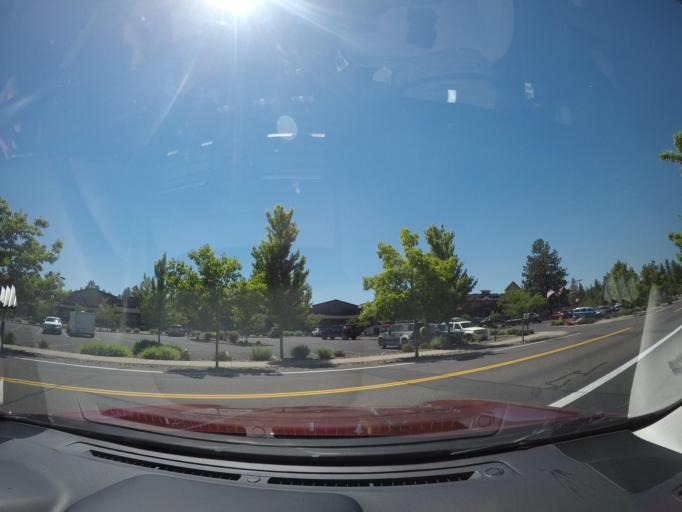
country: US
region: Oregon
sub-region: Deschutes County
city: Sisters
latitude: 44.2966
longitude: -121.5612
